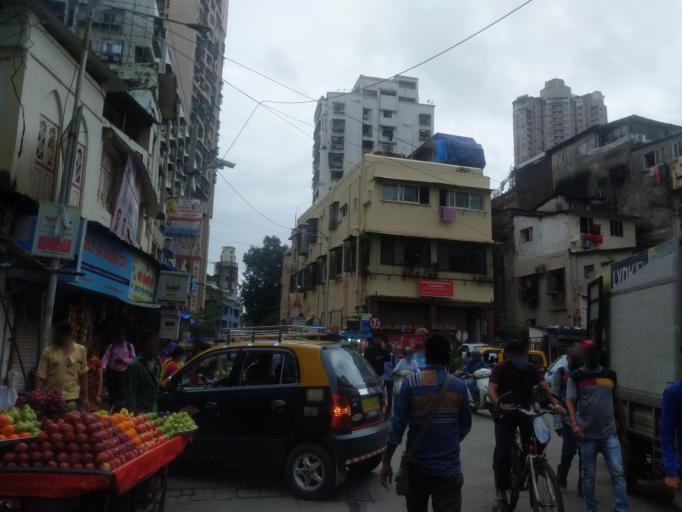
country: IN
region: Maharashtra
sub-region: Mumbai Suburban
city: Mumbai
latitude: 18.9537
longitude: 72.8267
